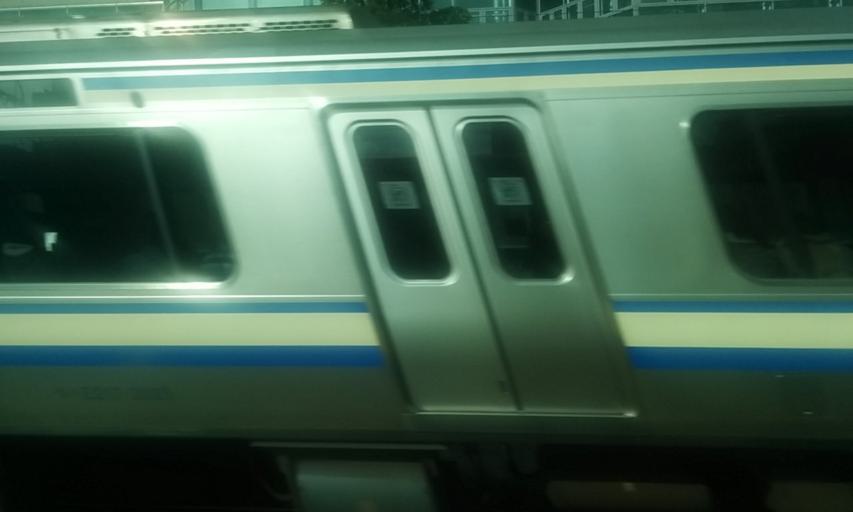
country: JP
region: Kanagawa
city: Yokohama
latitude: 35.4319
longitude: 139.5566
